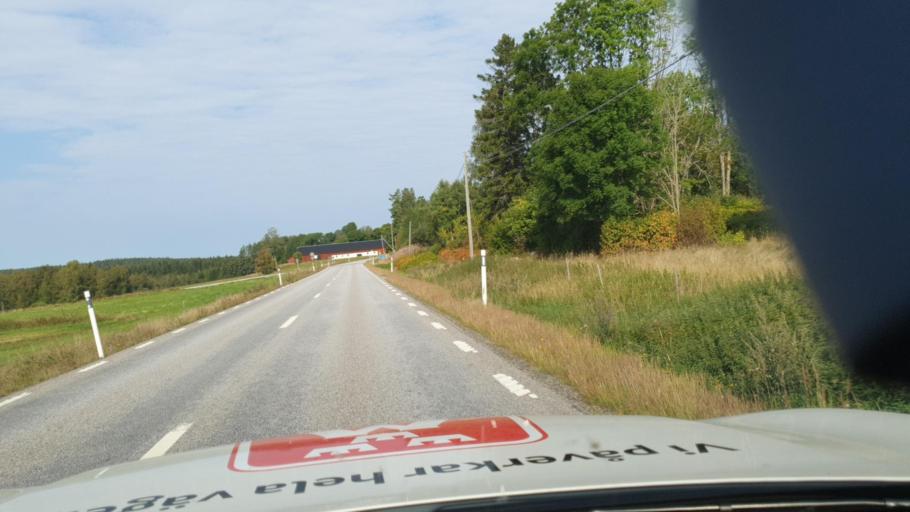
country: SE
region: Vaestra Goetaland
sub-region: Dals-Ed Kommun
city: Ed
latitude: 58.8792
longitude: 11.9910
